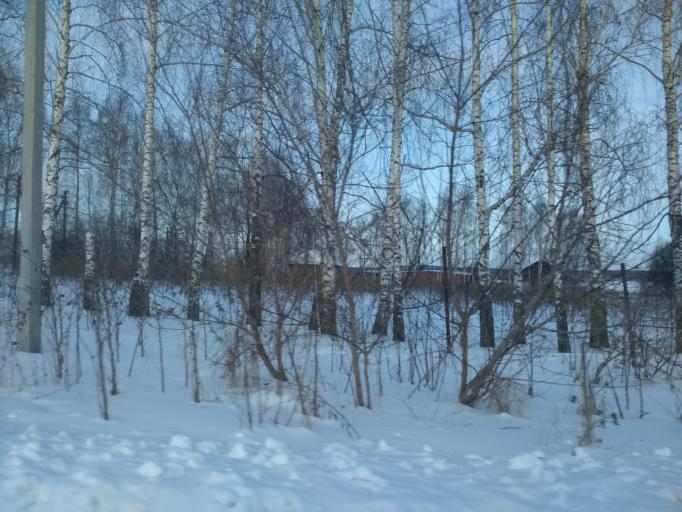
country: RU
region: Bashkortostan
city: Iglino
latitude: 54.7753
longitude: 56.5431
